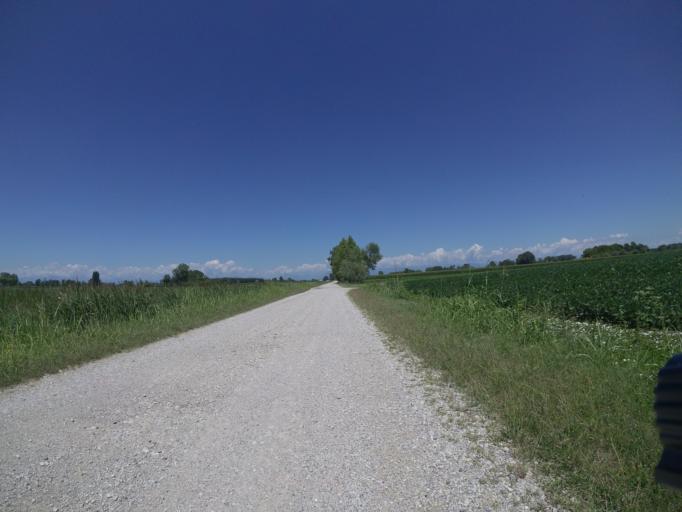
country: IT
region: Friuli Venezia Giulia
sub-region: Provincia di Udine
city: Talmassons
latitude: 45.9045
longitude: 13.1044
